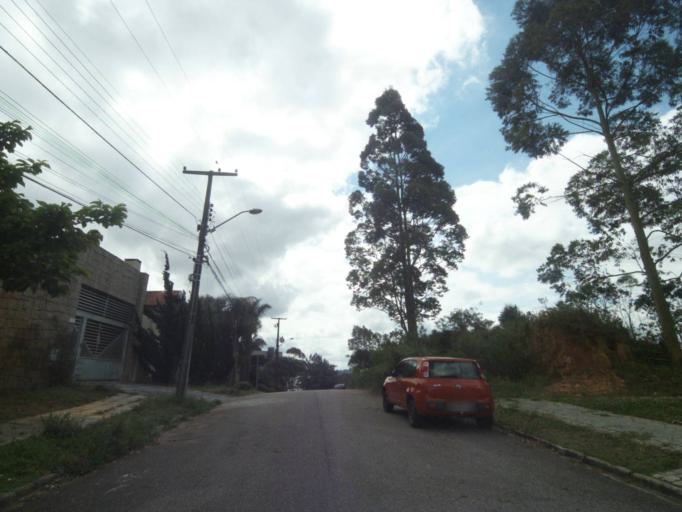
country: BR
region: Parana
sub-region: Curitiba
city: Curitiba
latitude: -25.3813
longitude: -49.2870
